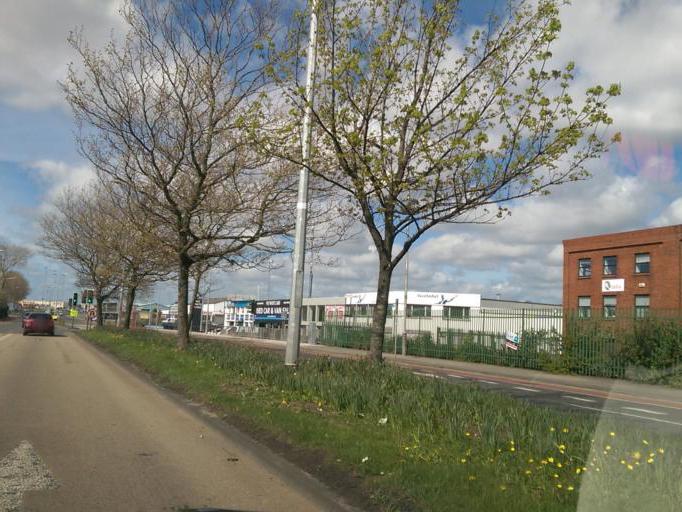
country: IE
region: Leinster
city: Crumlin
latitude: 53.3236
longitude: -6.3452
